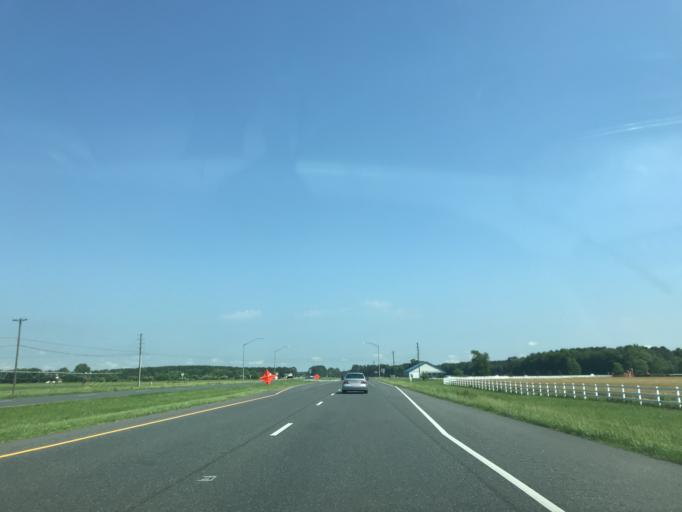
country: US
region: Maryland
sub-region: Wicomico County
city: Hebron
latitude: 38.4487
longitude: -75.7007
